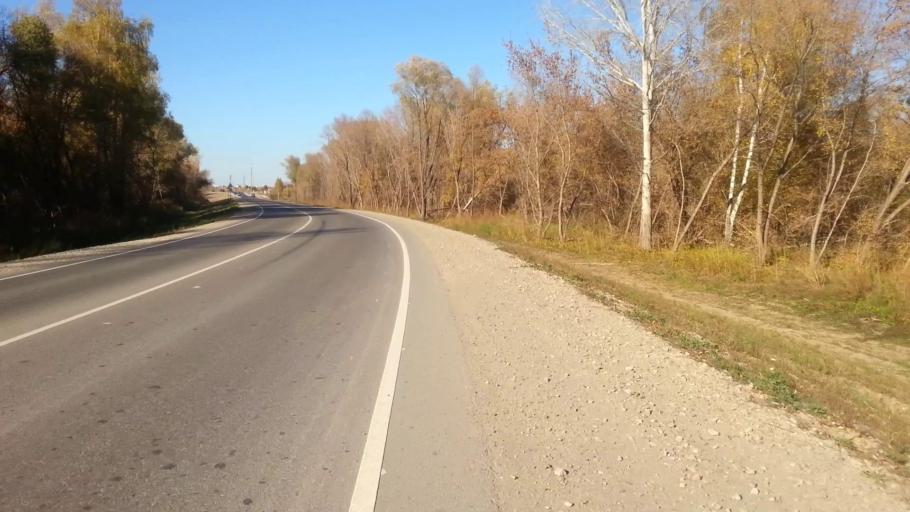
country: RU
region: Altai Krai
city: Sannikovo
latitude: 53.3233
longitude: 83.9430
